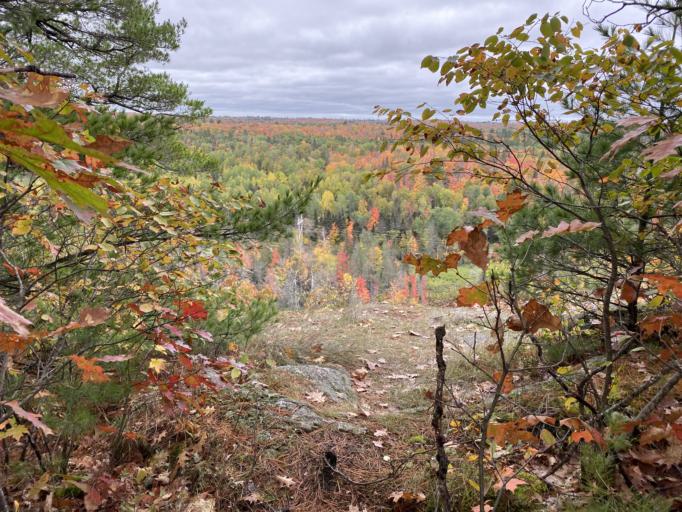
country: US
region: Michigan
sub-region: Marquette County
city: West Ishpeming
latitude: 46.5387
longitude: -87.9958
